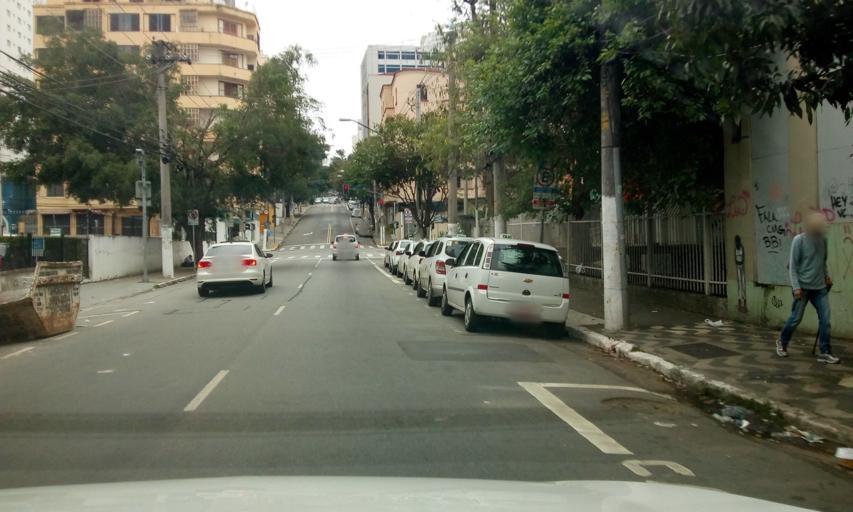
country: BR
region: Sao Paulo
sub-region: Sao Paulo
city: Sao Paulo
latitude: -23.5333
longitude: -46.6648
